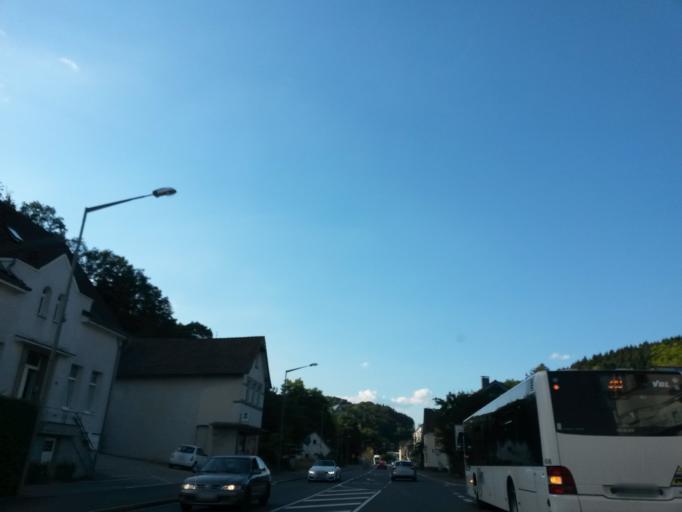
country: DE
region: North Rhine-Westphalia
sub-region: Regierungsbezirk Koln
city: Gummersbach
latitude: 51.0073
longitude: 7.5722
